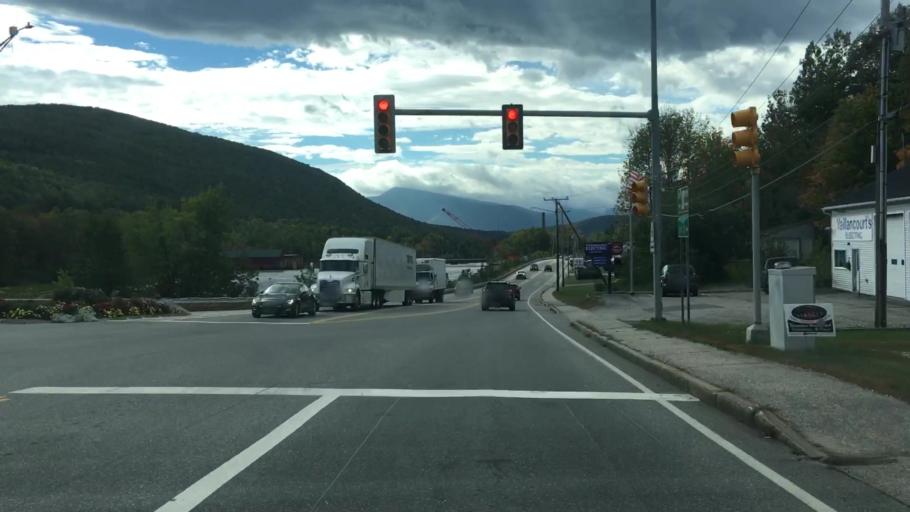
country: US
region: New Hampshire
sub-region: Coos County
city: Berlin
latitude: 44.4608
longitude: -71.1867
